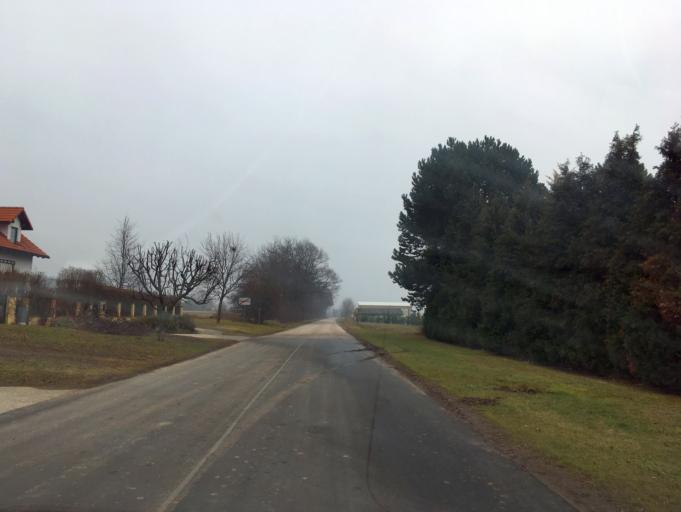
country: AT
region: Lower Austria
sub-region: Politischer Bezirk Bruck an der Leitha
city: Trautmannsdorf an der Leitha
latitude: 48.0395
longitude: 16.6780
